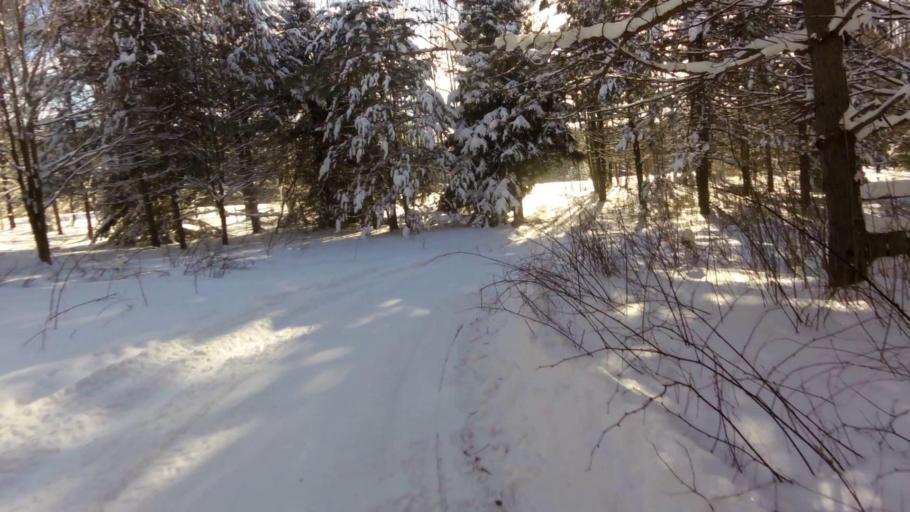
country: US
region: New York
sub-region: Chautauqua County
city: Falconer
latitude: 42.2559
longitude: -79.1690
